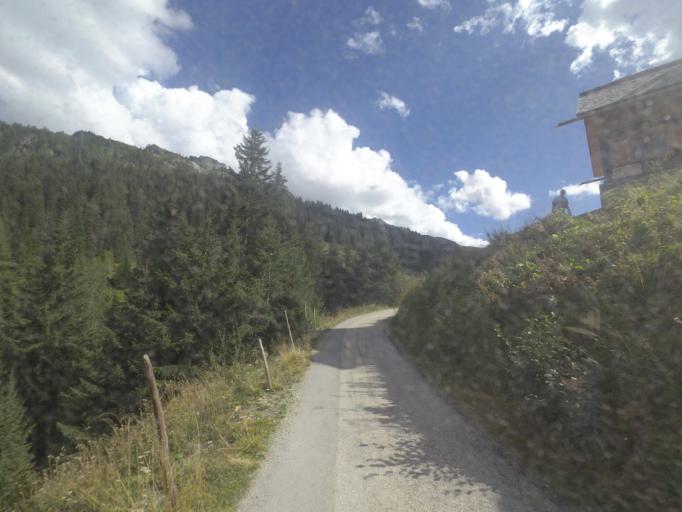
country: AT
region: Salzburg
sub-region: Politischer Bezirk Sankt Johann im Pongau
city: Kleinarl
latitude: 47.1806
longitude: 13.3551
